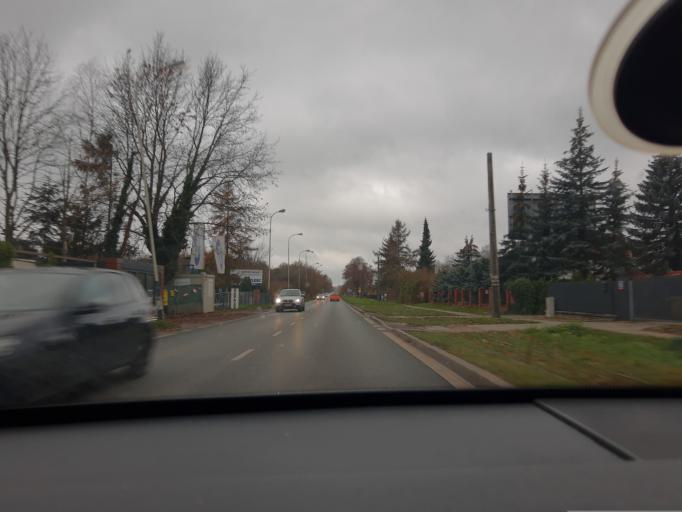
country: PL
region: Lodz Voivodeship
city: Lodz
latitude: 51.7605
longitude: 19.4020
